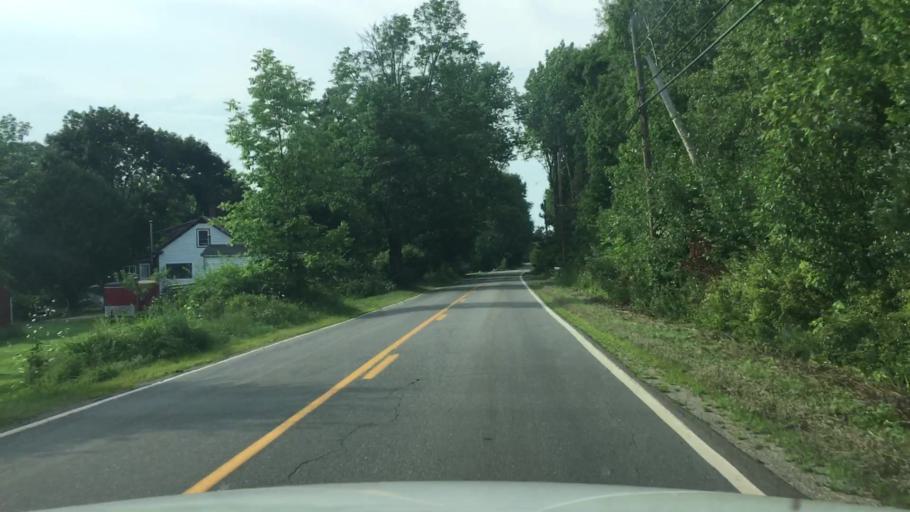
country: US
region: Maine
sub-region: Lincoln County
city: Waldoboro
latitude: 44.1573
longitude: -69.3762
